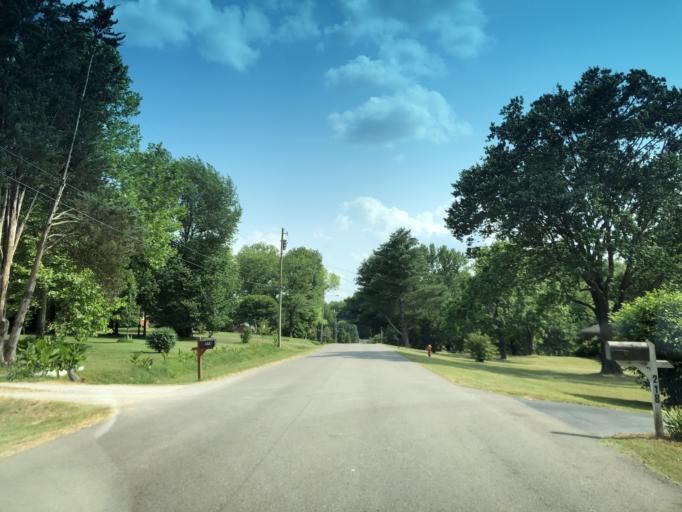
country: US
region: Tennessee
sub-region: Davidson County
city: Goodlettsville
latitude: 36.2592
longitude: -86.7235
